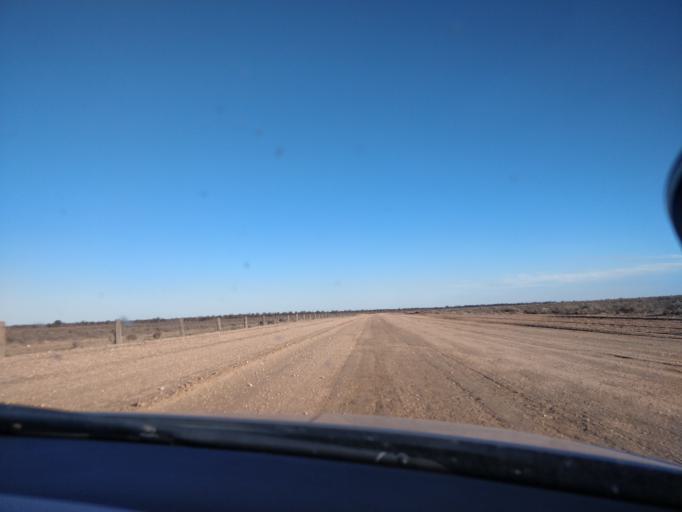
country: AU
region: New South Wales
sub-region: Wentworth
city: Gol Gol
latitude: -33.8305
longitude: 142.8989
